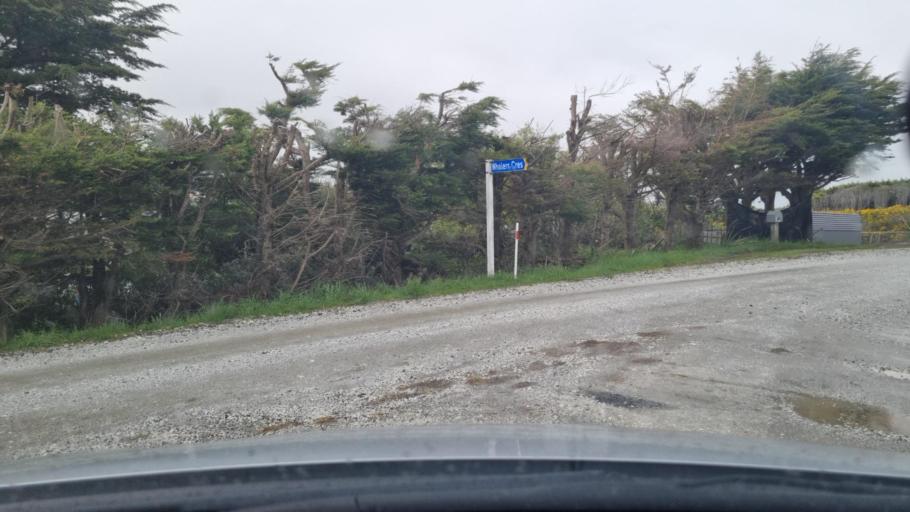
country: NZ
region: Southland
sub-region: Invercargill City
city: Bluff
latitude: -46.5179
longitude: 168.2596
